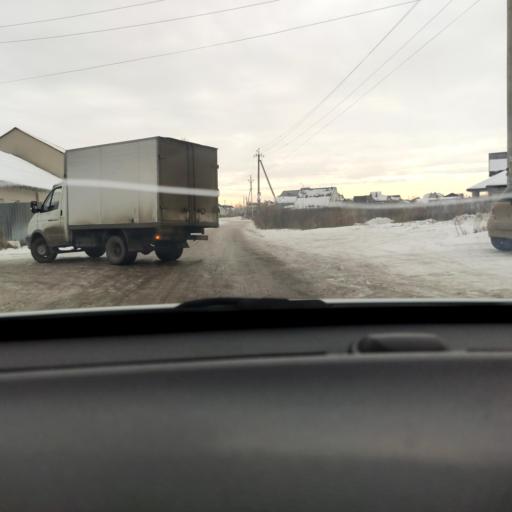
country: RU
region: Voronezj
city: Novaya Usman'
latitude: 51.6673
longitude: 39.3363
